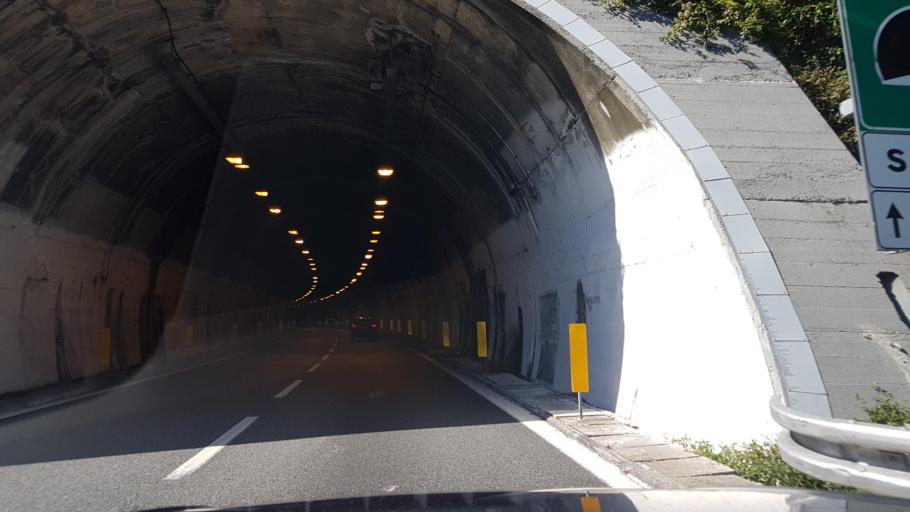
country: IT
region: Liguria
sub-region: Provincia di Savona
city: Vezzi Portio
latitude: 44.2284
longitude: 8.3689
